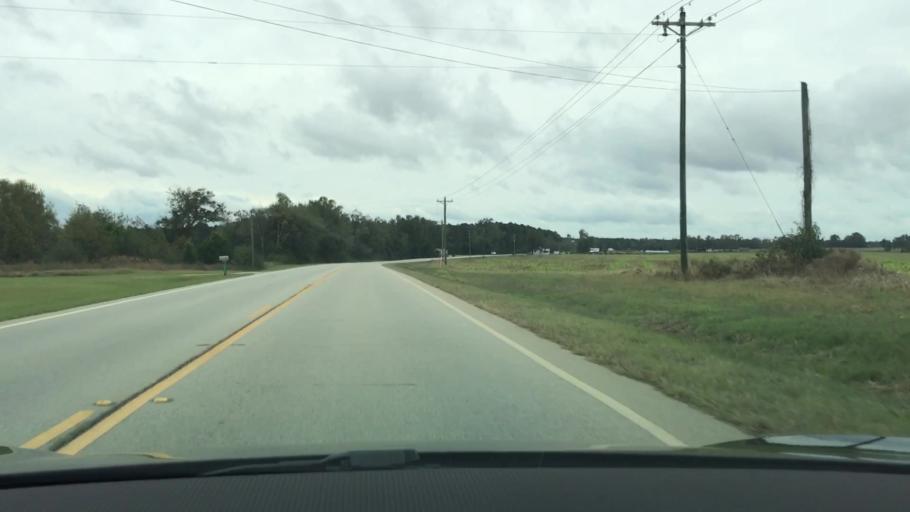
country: US
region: Georgia
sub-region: Jefferson County
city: Wrens
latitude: 33.1820
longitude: -82.4539
